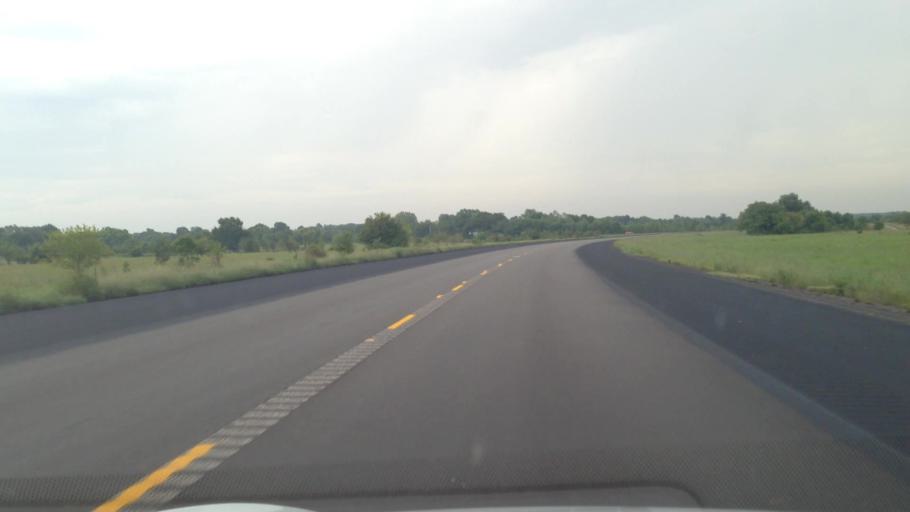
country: US
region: Kansas
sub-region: Cherokee County
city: Baxter Springs
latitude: 37.0488
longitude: -94.7161
